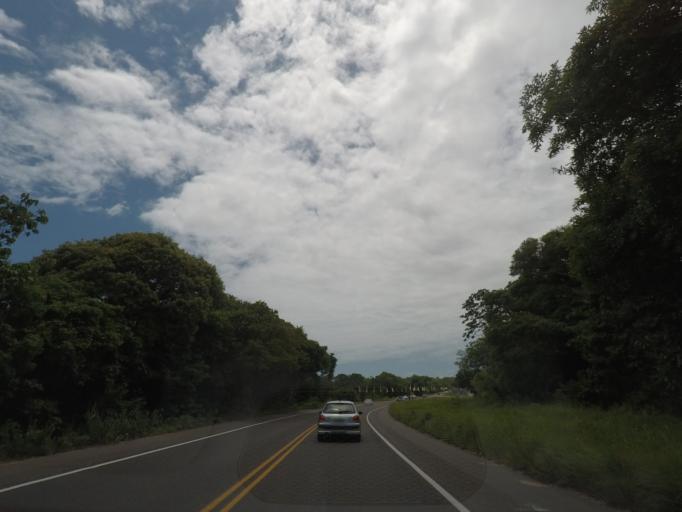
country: BR
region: Bahia
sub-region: Itaparica
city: Itaparica
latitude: -12.9594
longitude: -38.6326
